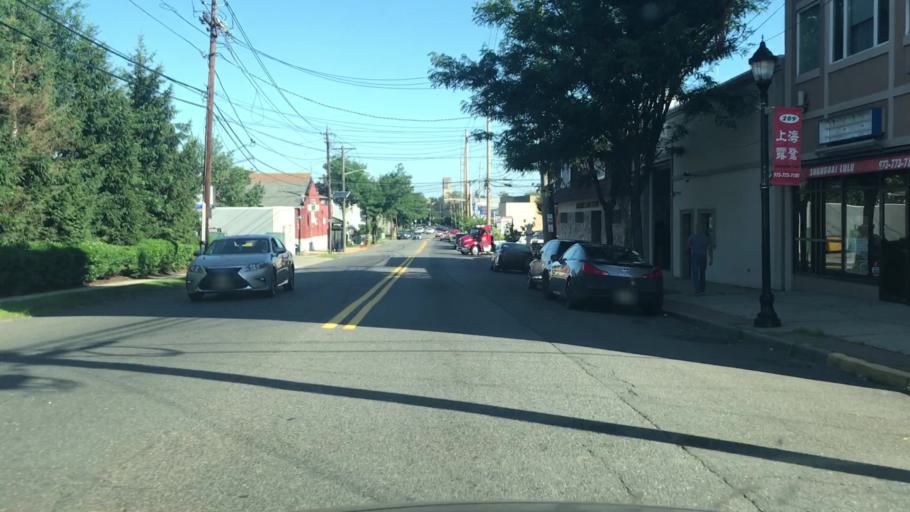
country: US
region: New Jersey
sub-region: Bergen County
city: Wallington
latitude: 40.8483
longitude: -74.1127
